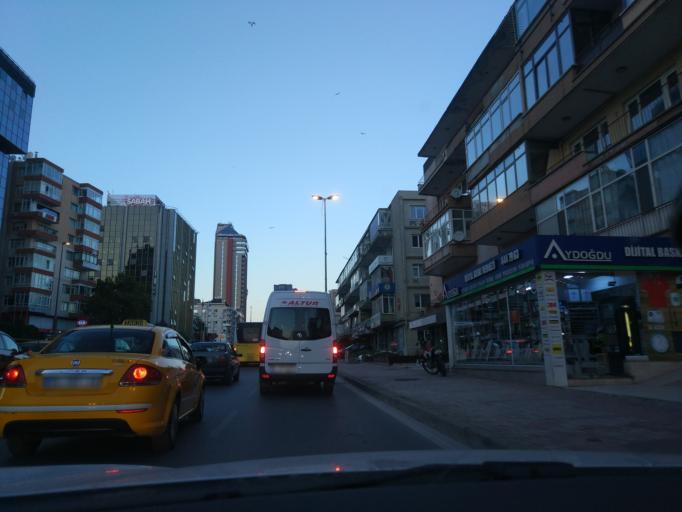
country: TR
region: Istanbul
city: Sisli
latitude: 41.0594
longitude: 29.0107
